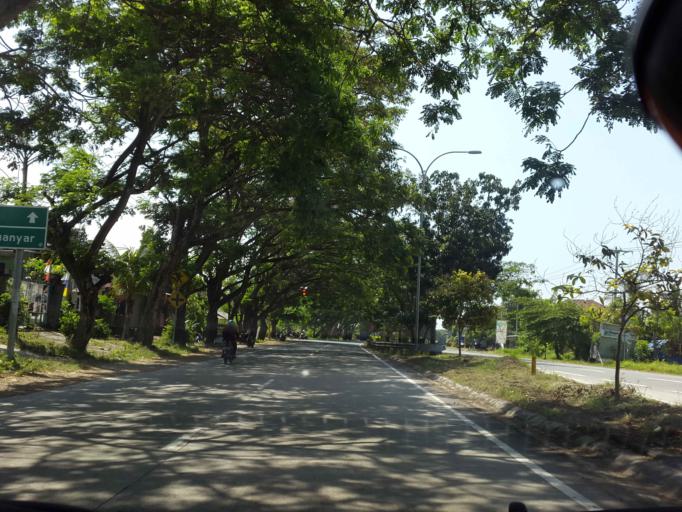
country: ID
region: Bali
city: Klungkung
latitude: -8.5683
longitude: 115.3737
